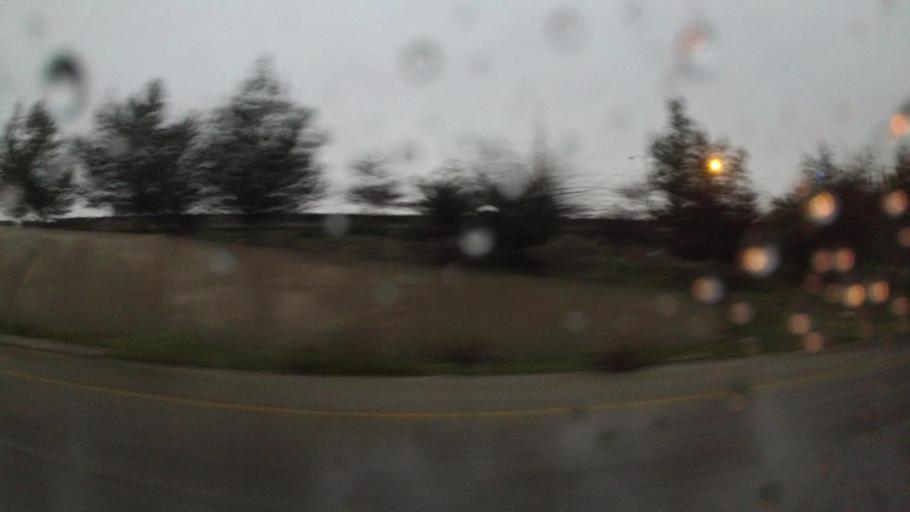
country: JO
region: Amman
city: Umm as Summaq
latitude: 31.9126
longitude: 35.8596
